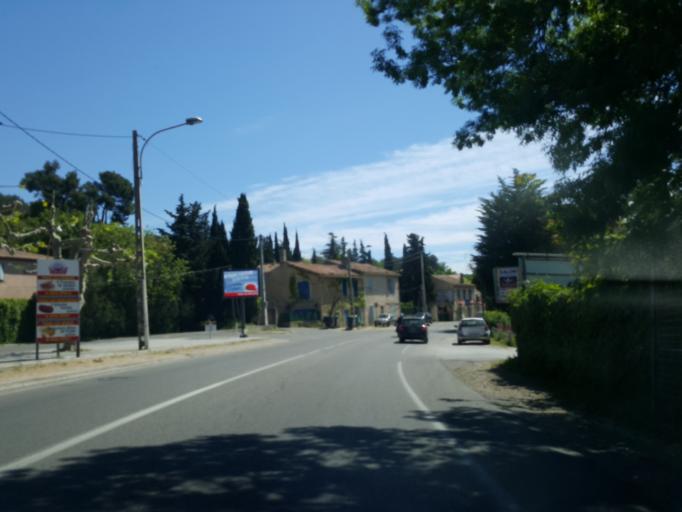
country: FR
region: Provence-Alpes-Cote d'Azur
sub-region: Departement des Bouches-du-Rhone
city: Roquevaire
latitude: 43.3440
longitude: 5.6037
